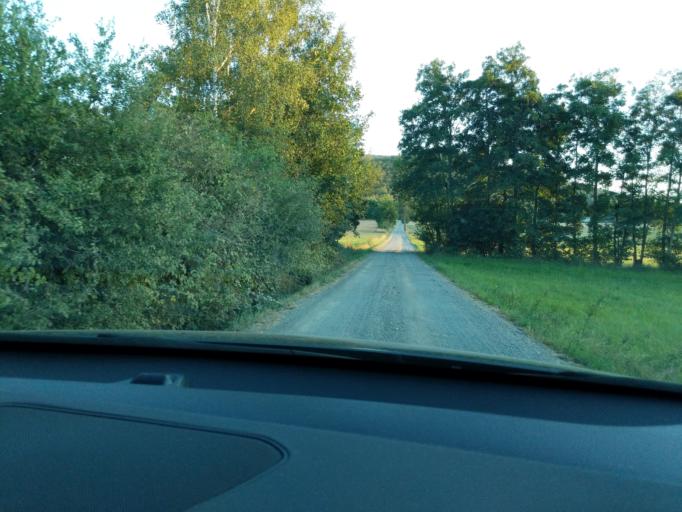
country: DE
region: Hesse
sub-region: Regierungsbezirk Kassel
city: Waldeck
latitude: 51.1838
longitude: 9.0309
